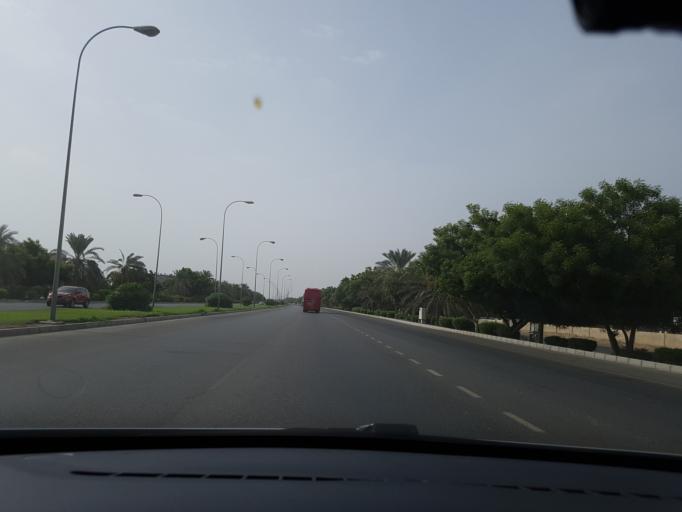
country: OM
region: Al Batinah
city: Al Sohar
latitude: 24.3695
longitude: 56.7054
